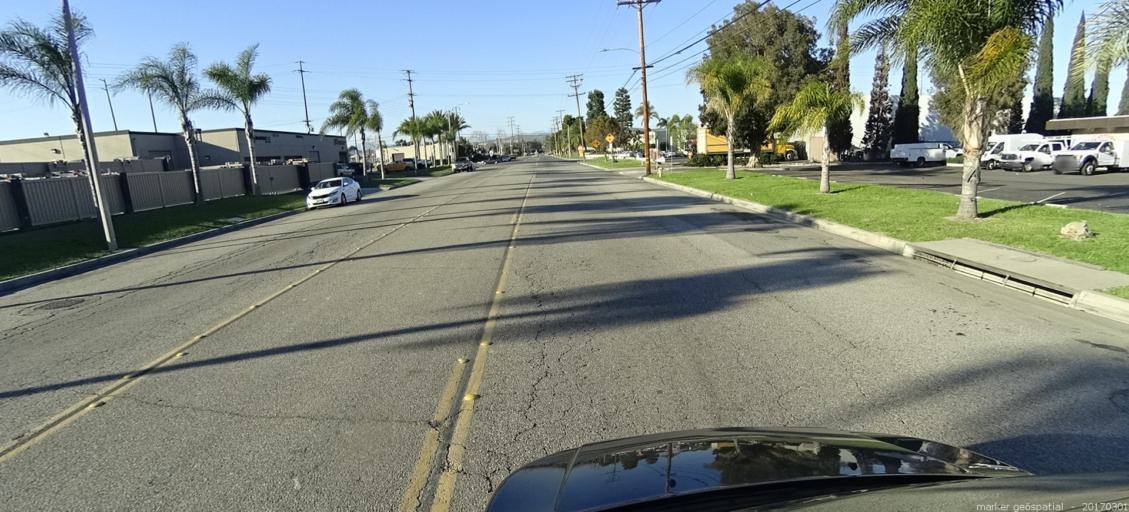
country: US
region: California
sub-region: Orange County
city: Placentia
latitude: 33.8616
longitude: -117.8370
